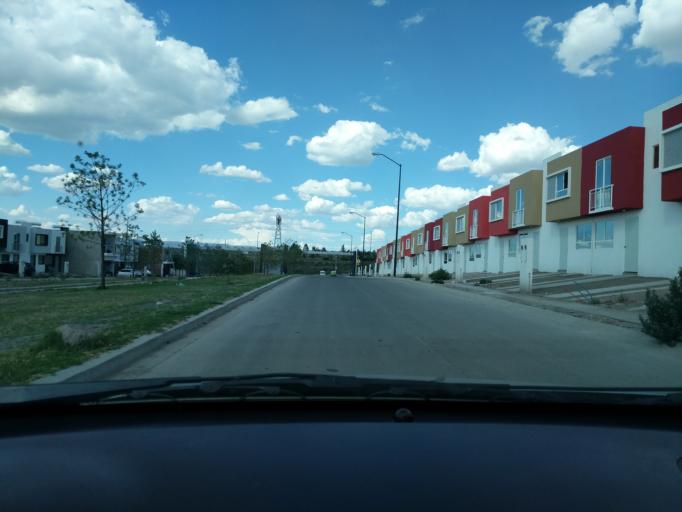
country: MX
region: Guanajuato
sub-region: Leon
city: Fraccionamiento Paseo de las Torres
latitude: 21.1716
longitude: -101.7651
